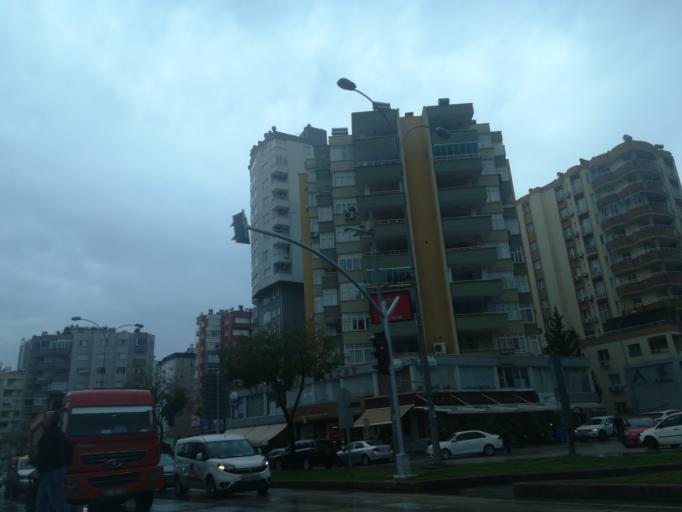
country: TR
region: Adana
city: Adana
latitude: 37.0477
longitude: 35.2990
